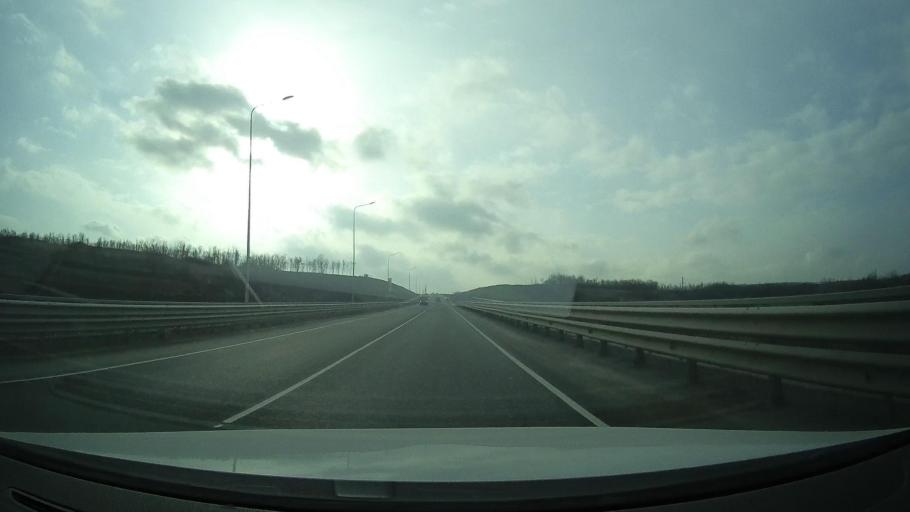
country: RU
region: Rostov
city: Grushevskaya
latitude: 47.4359
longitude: 39.8708
